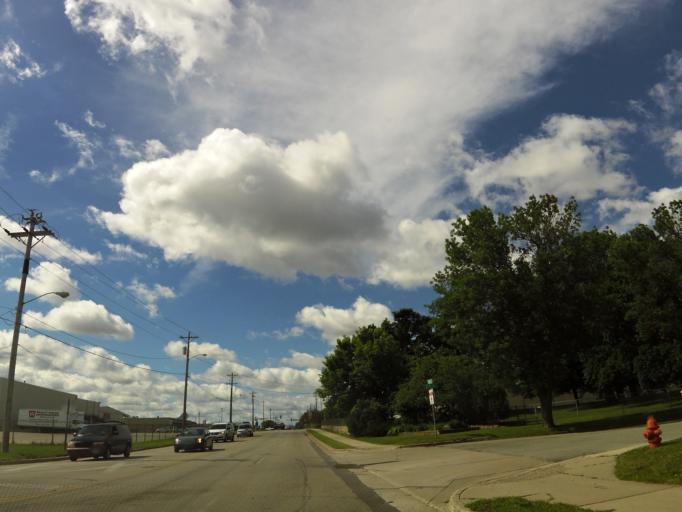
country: US
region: Minnesota
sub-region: Olmsted County
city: Rochester
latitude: 44.0025
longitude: -92.4587
